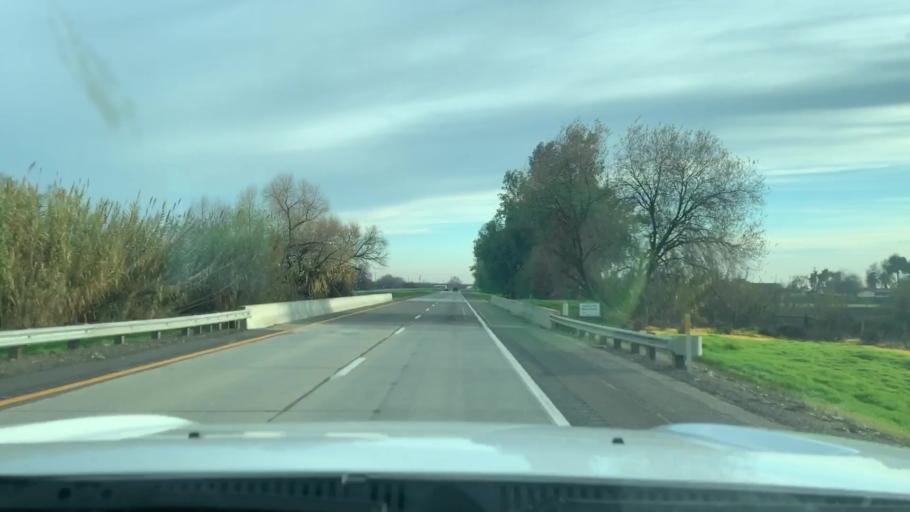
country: US
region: California
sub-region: Kings County
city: Lemoore
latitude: 36.3631
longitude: -119.8099
